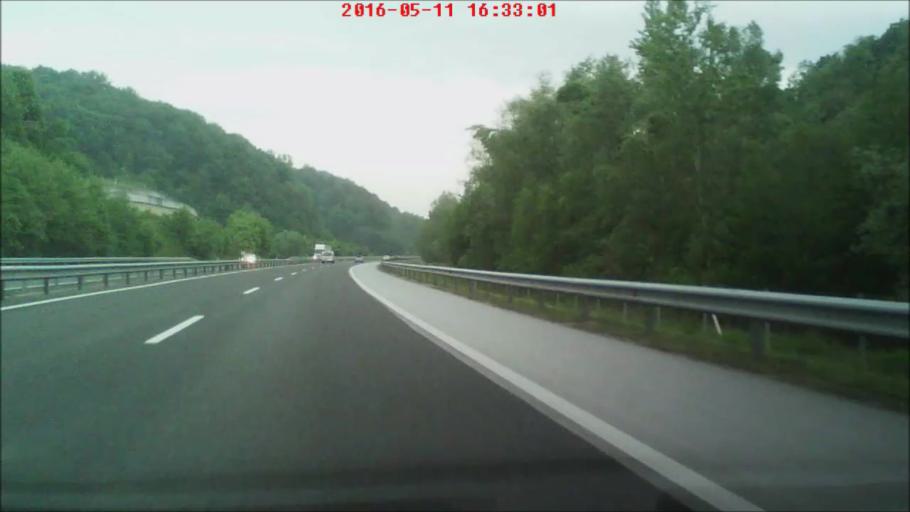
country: SI
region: Pesnica
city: Pesnica pri Mariboru
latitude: 46.6358
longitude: 15.6557
